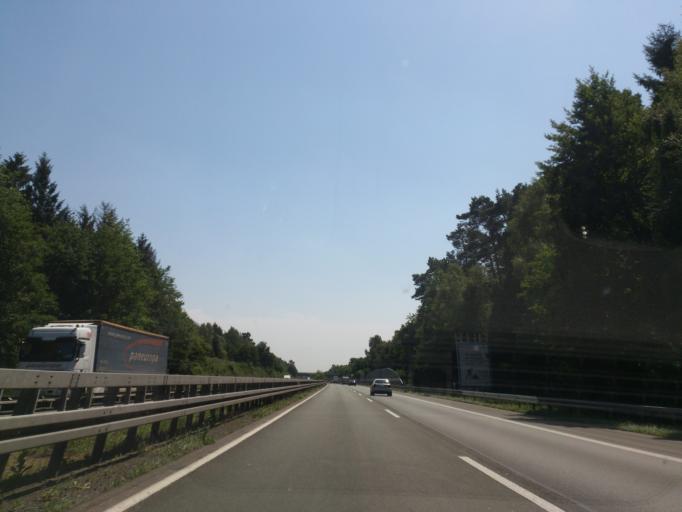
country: DE
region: North Rhine-Westphalia
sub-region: Regierungsbezirk Detmold
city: Hovelhof
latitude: 51.8838
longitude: 8.6448
